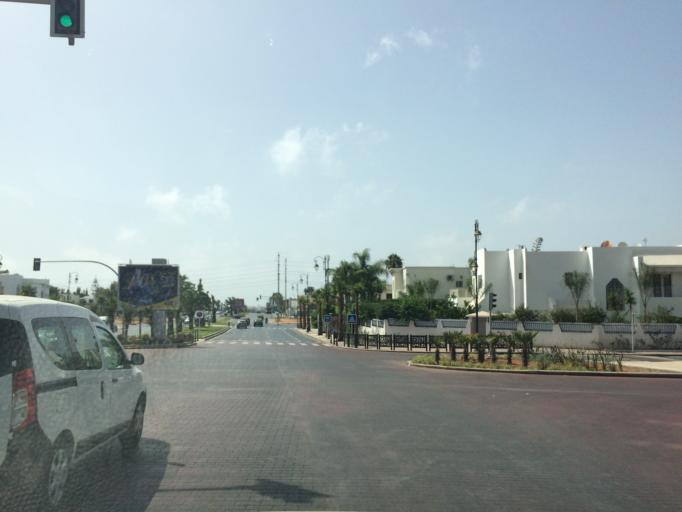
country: MA
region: Rabat-Sale-Zemmour-Zaer
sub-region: Skhirate-Temara
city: Temara
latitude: 33.9600
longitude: -6.8732
